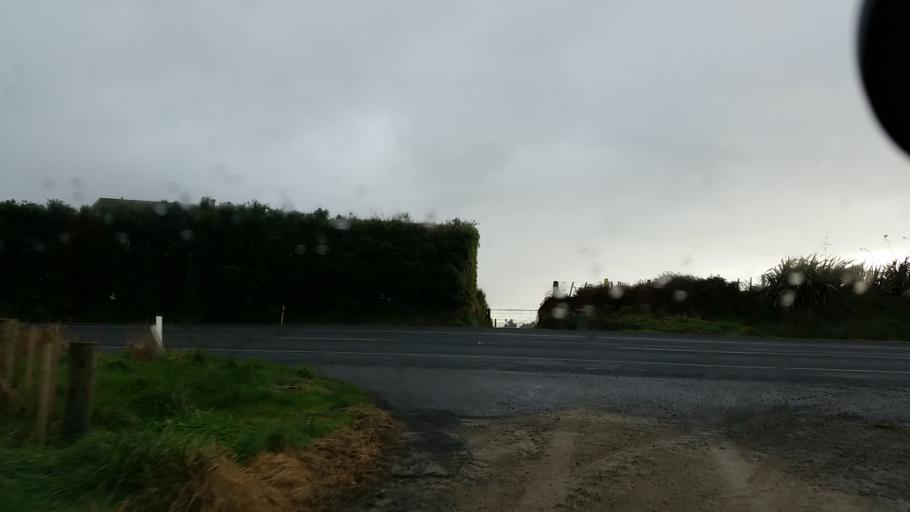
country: NZ
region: Taranaki
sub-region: South Taranaki District
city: Patea
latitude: -39.7638
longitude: 174.6425
